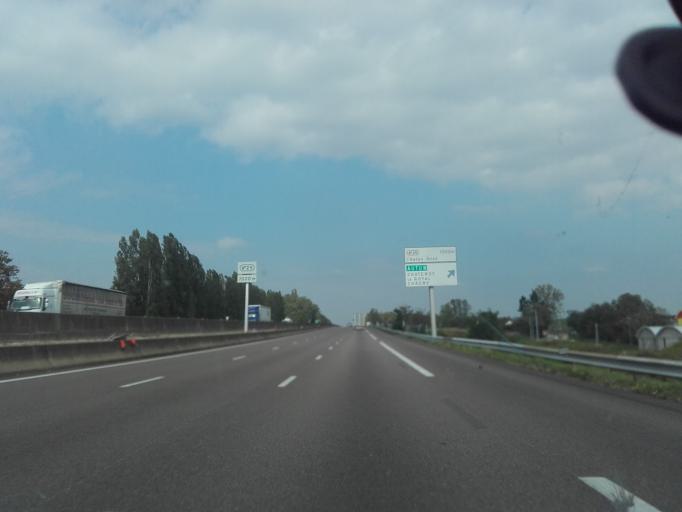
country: FR
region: Bourgogne
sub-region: Departement de Saone-et-Loire
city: Chatenoy-le-Royal
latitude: 46.7900
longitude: 4.8207
